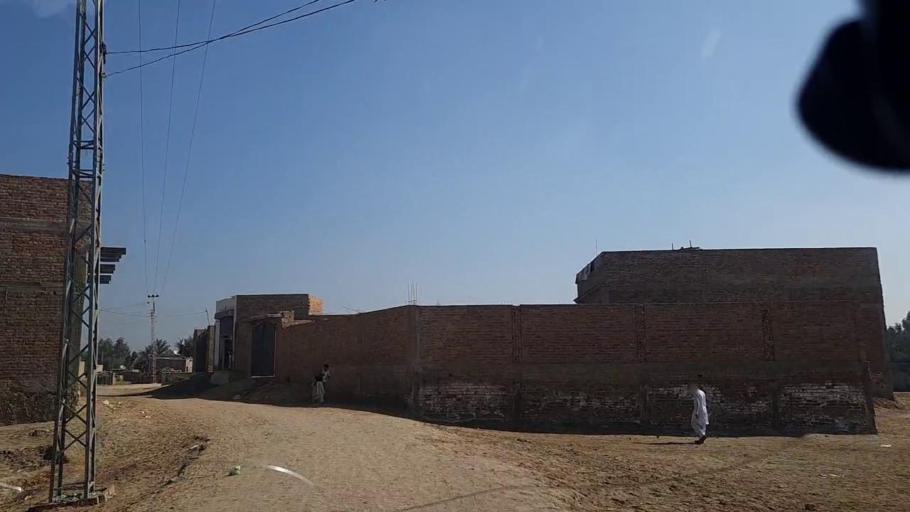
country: PK
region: Sindh
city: Khanpur
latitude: 27.8514
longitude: 69.4195
